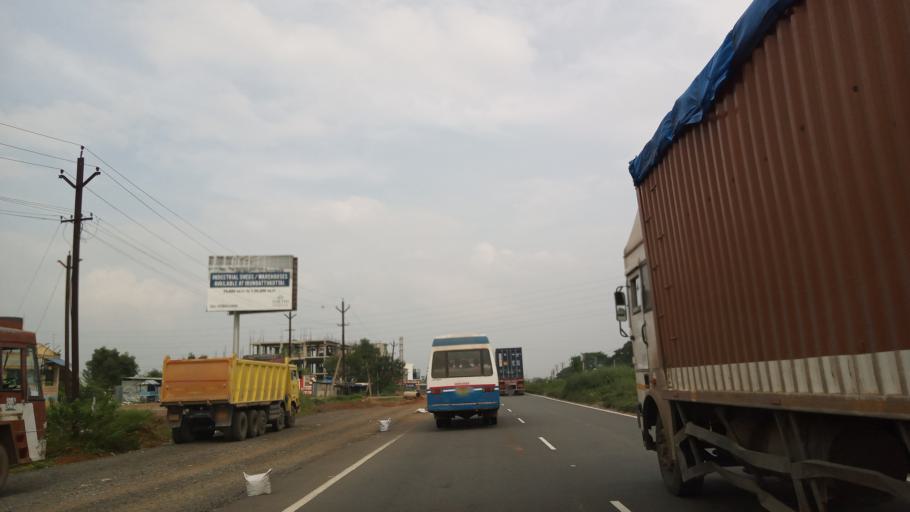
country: IN
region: Tamil Nadu
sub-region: Kancheepuram
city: Sriperumbudur
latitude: 12.9379
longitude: 79.9132
